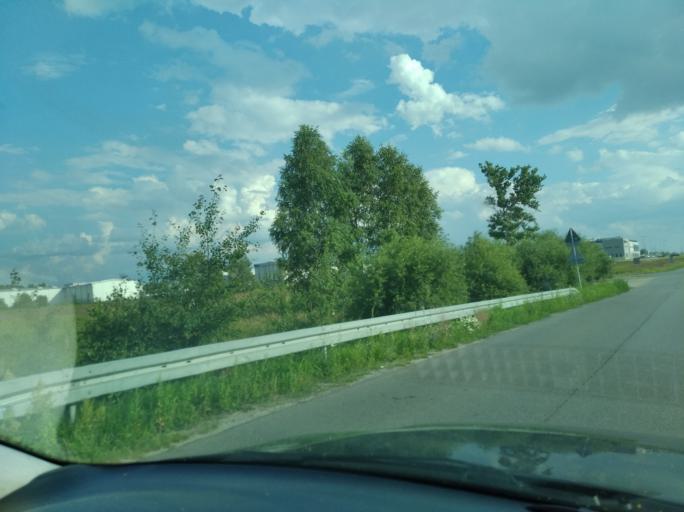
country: PL
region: Subcarpathian Voivodeship
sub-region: Powiat rzeszowski
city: Wysoka Glogowska
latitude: 50.1257
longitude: 22.0252
